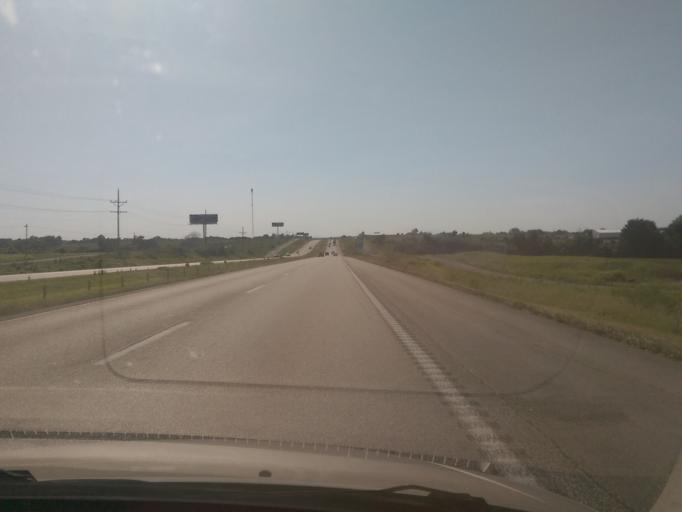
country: US
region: Missouri
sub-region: Saline County
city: Sweet Springs
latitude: 38.9797
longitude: -93.4695
